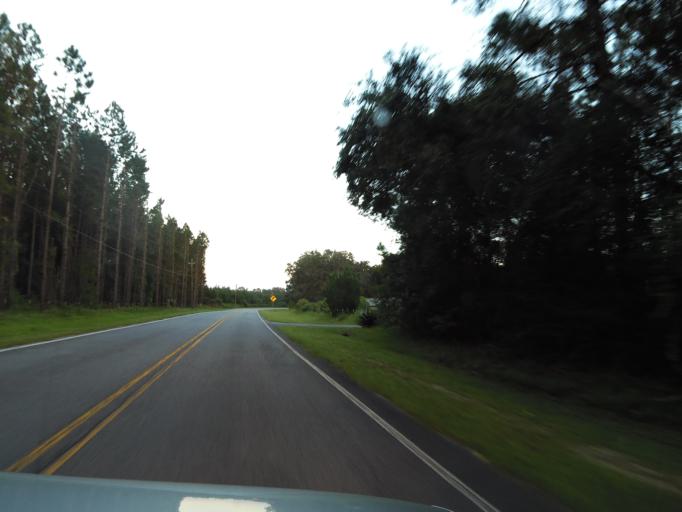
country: US
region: Georgia
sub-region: Camden County
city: Kingsland
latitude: 30.7736
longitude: -81.7006
